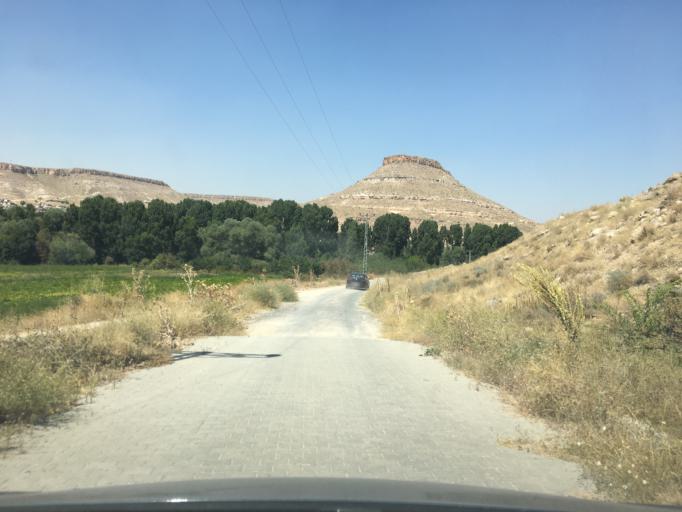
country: TR
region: Kayseri
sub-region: Yesilhisar
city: Yesilhisar
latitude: 38.4652
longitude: 34.9651
